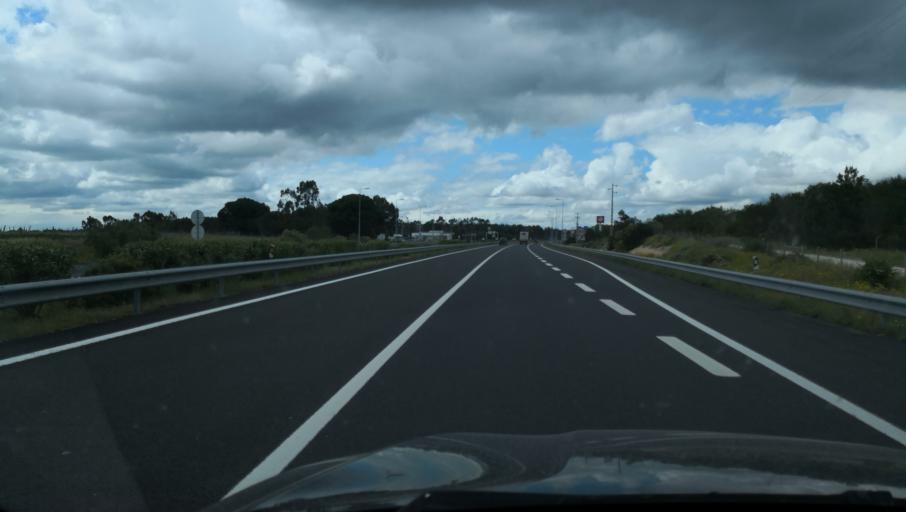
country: PT
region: Santarem
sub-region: Benavente
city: Poceirao
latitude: 38.7235
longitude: -8.6667
